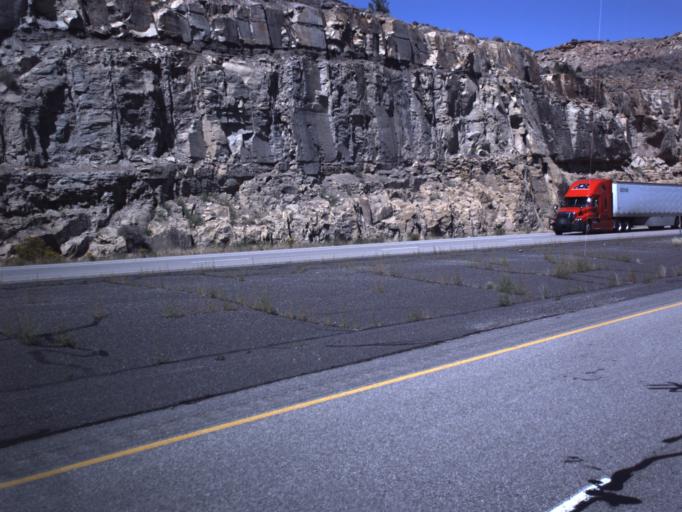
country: US
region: Utah
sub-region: Emery County
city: Ferron
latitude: 38.8030
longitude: -111.2650
